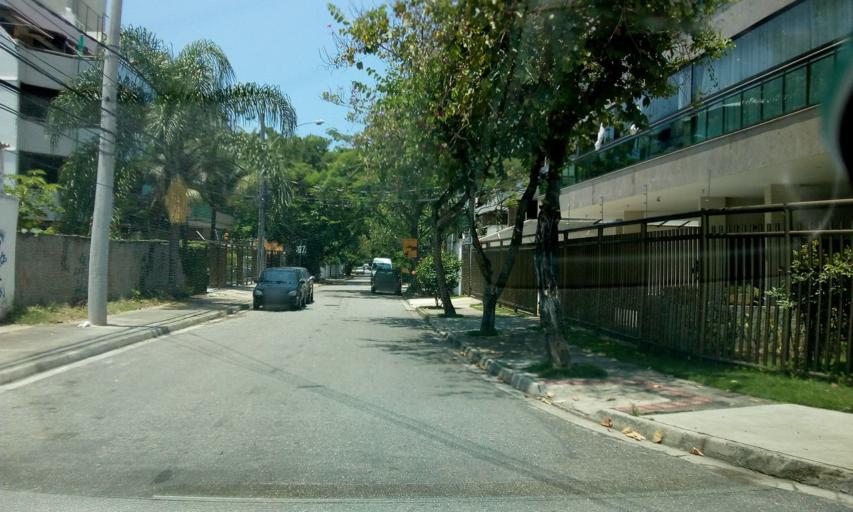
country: BR
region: Rio de Janeiro
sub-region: Nilopolis
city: Nilopolis
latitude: -23.0188
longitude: -43.4628
